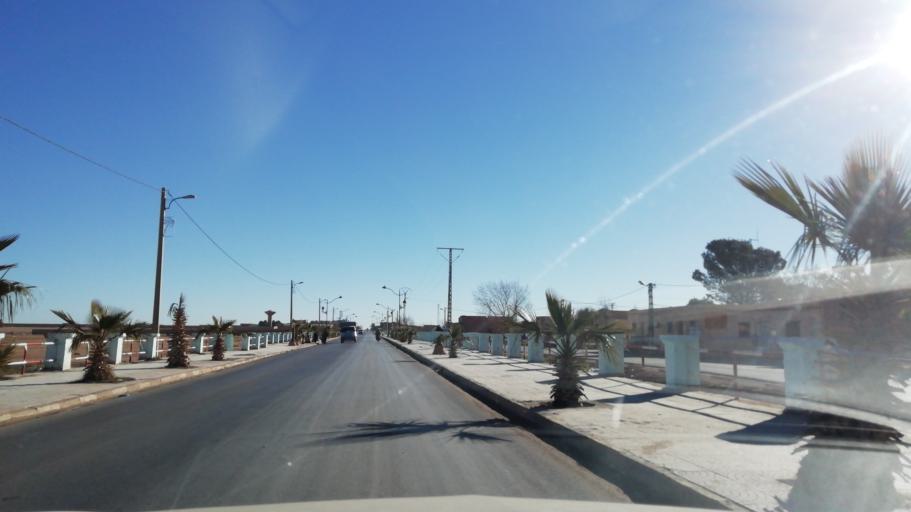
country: DZ
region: El Bayadh
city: El Bayadh
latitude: 33.8530
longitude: 0.6335
